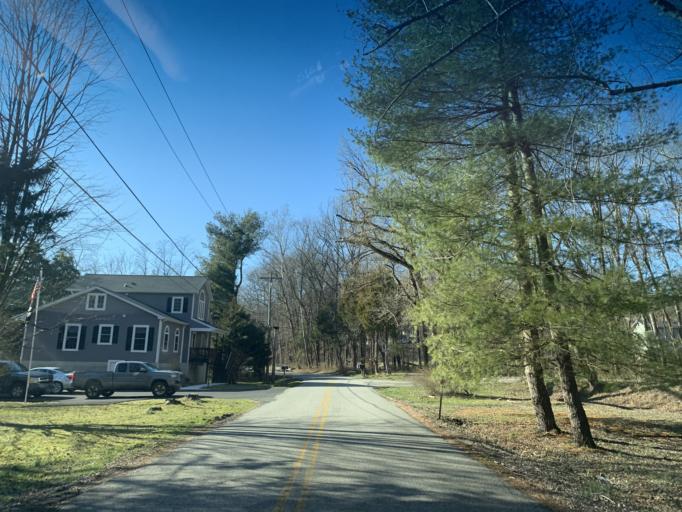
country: US
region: Maryland
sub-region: Cecil County
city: Rising Sun
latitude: 39.6556
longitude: -76.1191
